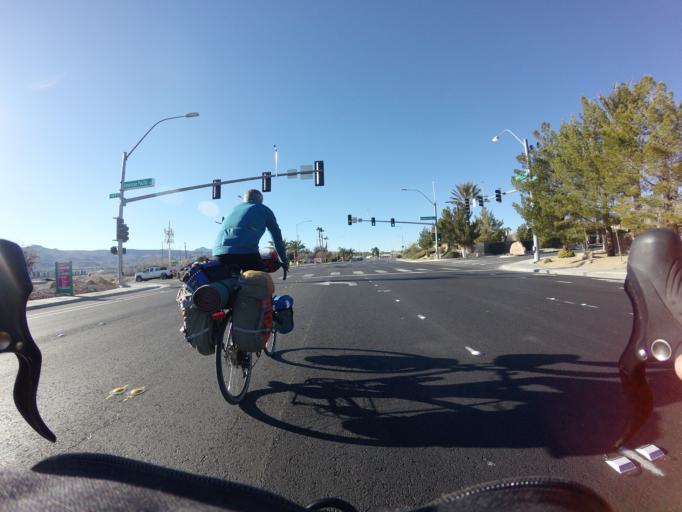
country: US
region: Nevada
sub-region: Clark County
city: Whitney
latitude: 36.0435
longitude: -115.0557
